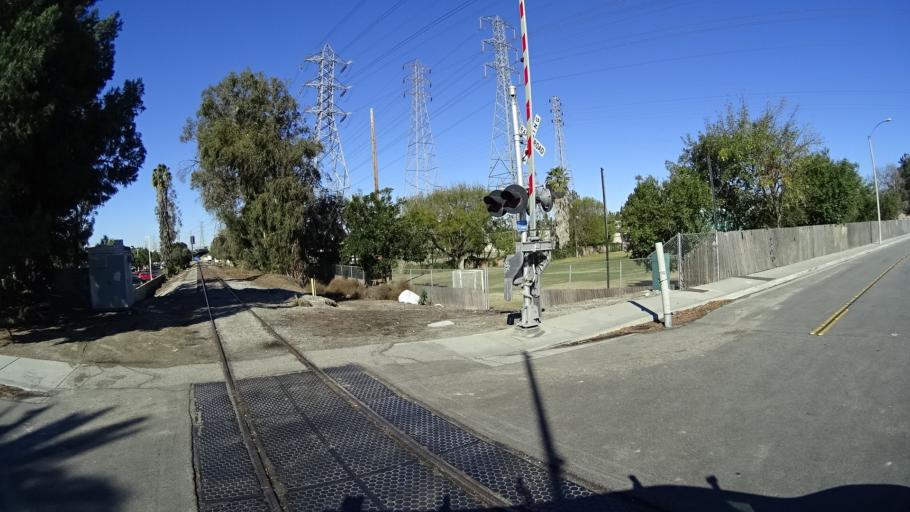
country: US
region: California
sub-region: Orange County
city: Orange
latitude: 33.8123
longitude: -117.8737
